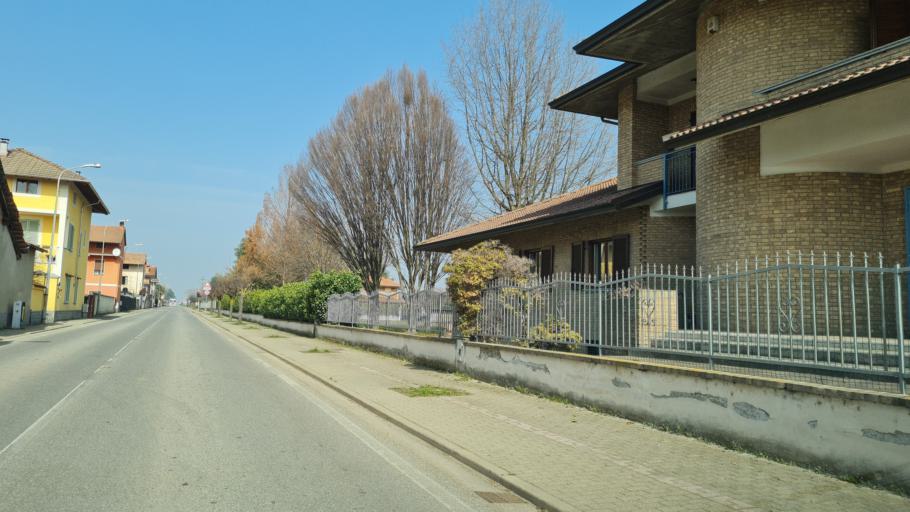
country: IT
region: Piedmont
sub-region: Provincia di Novara
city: Landiona
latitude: 45.4999
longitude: 8.4225
